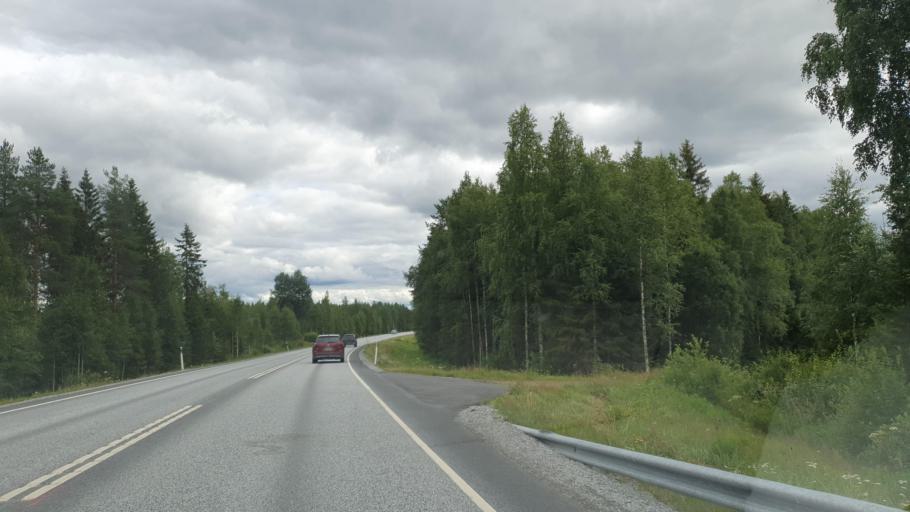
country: FI
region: Northern Savo
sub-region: Ylae-Savo
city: Sonkajaervi
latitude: 63.8871
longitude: 27.4347
